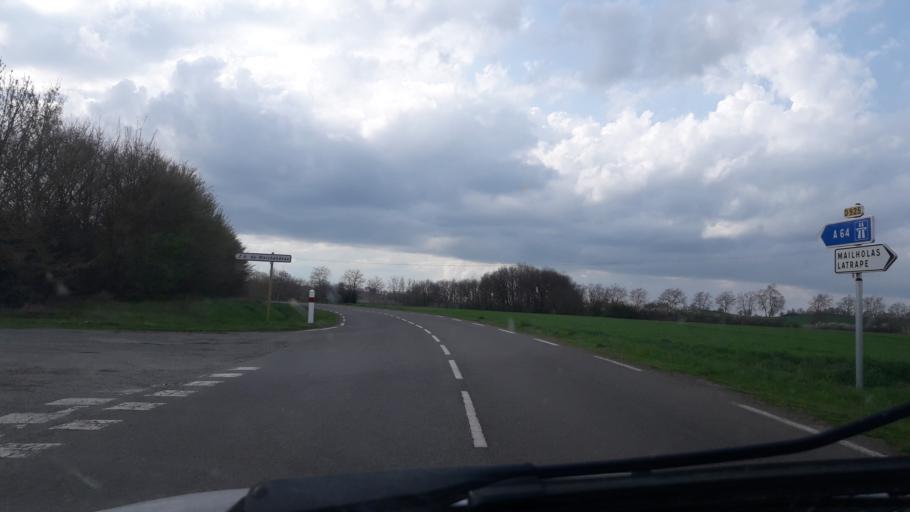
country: FR
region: Midi-Pyrenees
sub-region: Departement de la Haute-Garonne
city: Rieux-Volvestre
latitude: 43.2669
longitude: 1.2009
